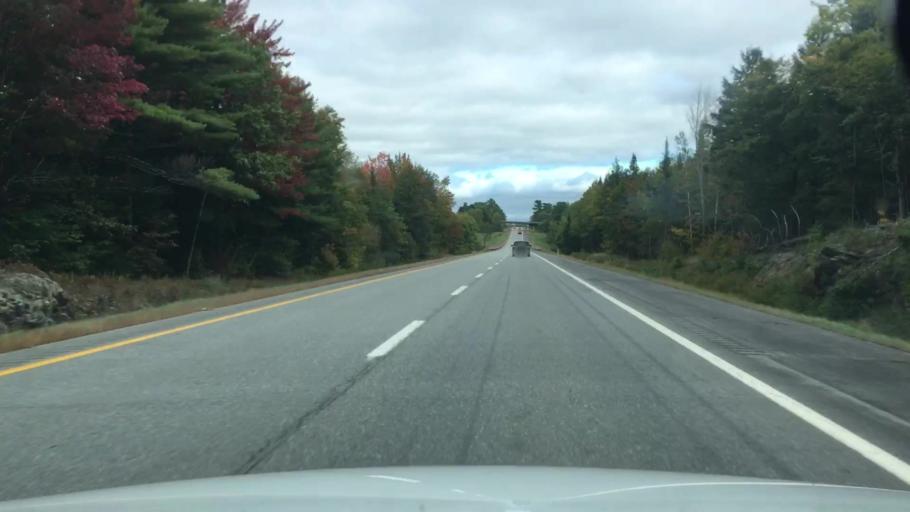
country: US
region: Maine
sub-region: Penobscot County
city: Carmel
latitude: 44.7793
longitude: -69.0705
